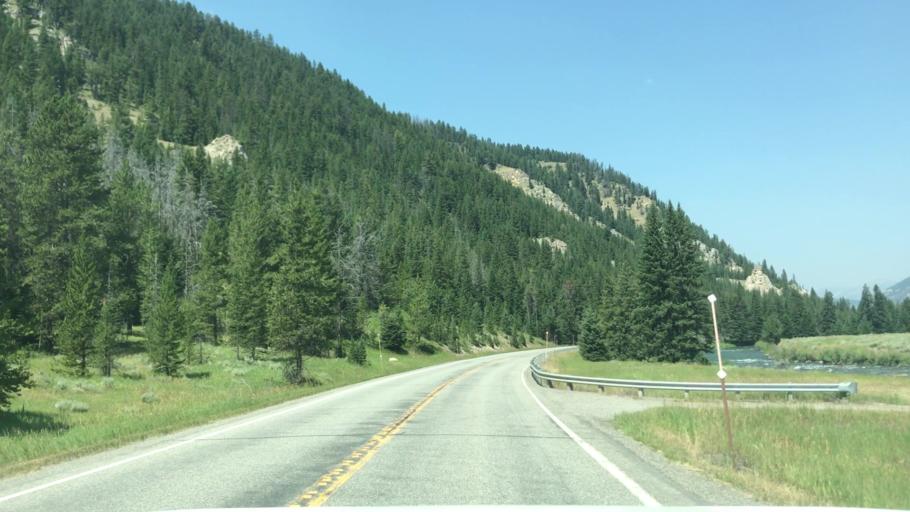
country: US
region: Montana
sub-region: Gallatin County
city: Big Sky
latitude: 45.0777
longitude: -111.2062
